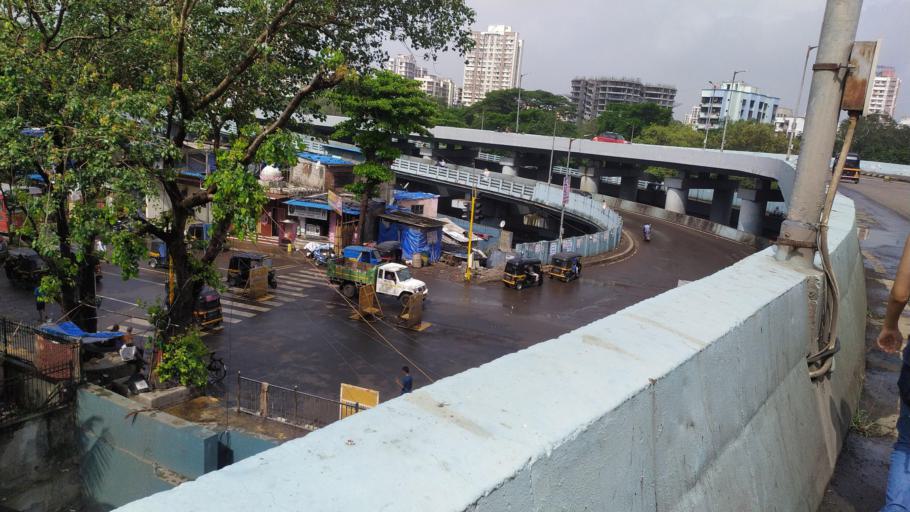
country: IN
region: Maharashtra
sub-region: Mumbai Suburban
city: Borivli
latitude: 19.2391
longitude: 72.8601
